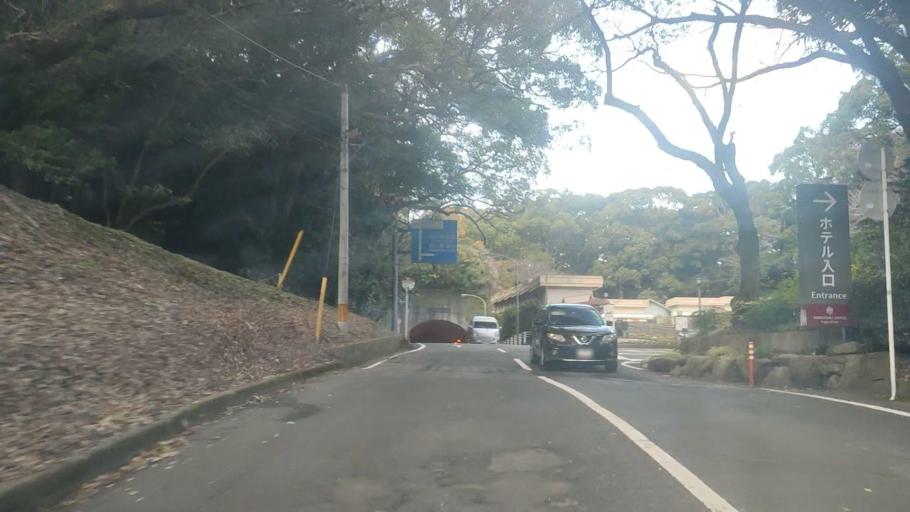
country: JP
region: Kagoshima
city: Kagoshima-shi
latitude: 31.5964
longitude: 130.5489
